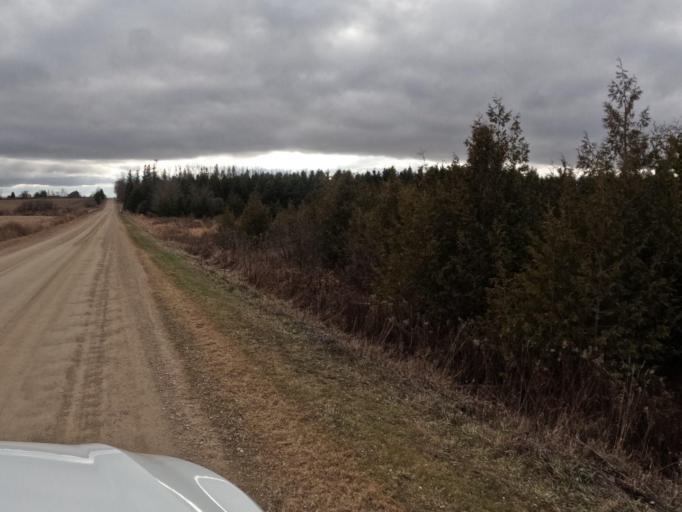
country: CA
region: Ontario
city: Shelburne
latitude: 43.8787
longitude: -80.3805
